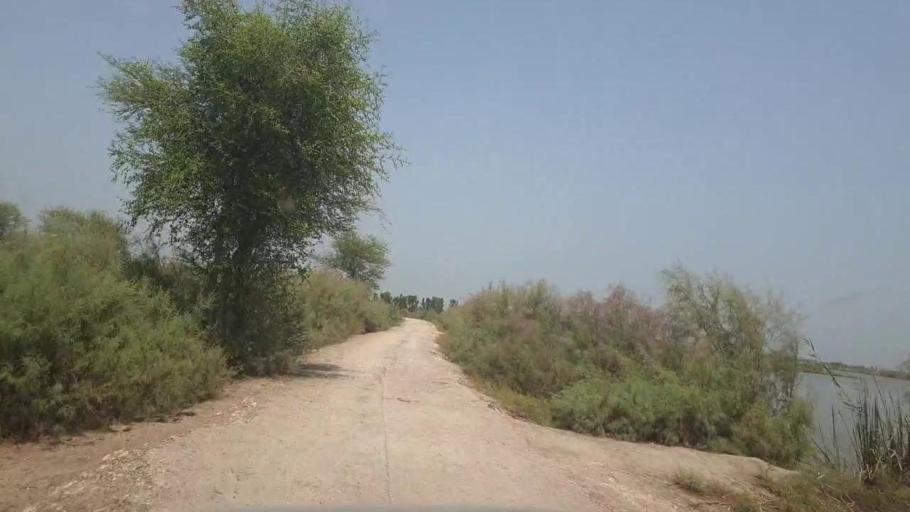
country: PK
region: Sindh
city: Lakhi
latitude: 27.8541
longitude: 68.6244
